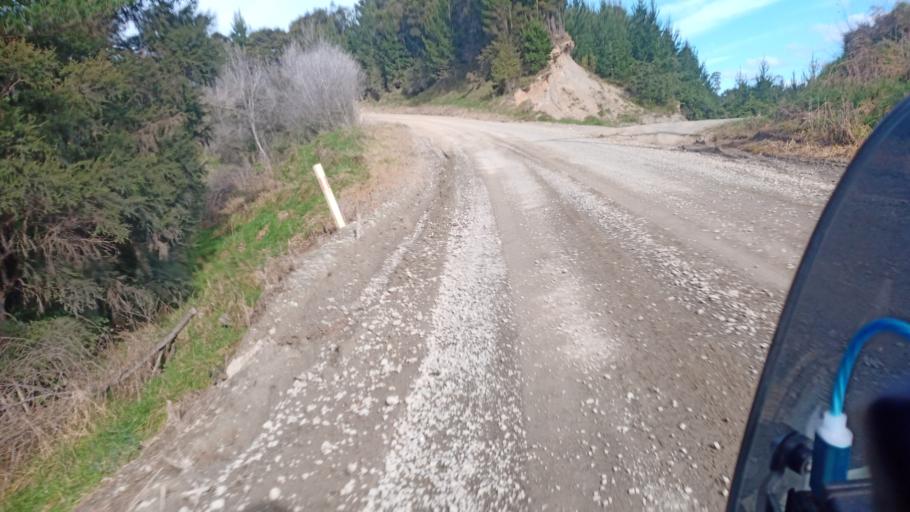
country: NZ
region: Gisborne
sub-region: Gisborne District
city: Gisborne
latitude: -38.1303
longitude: 178.1860
